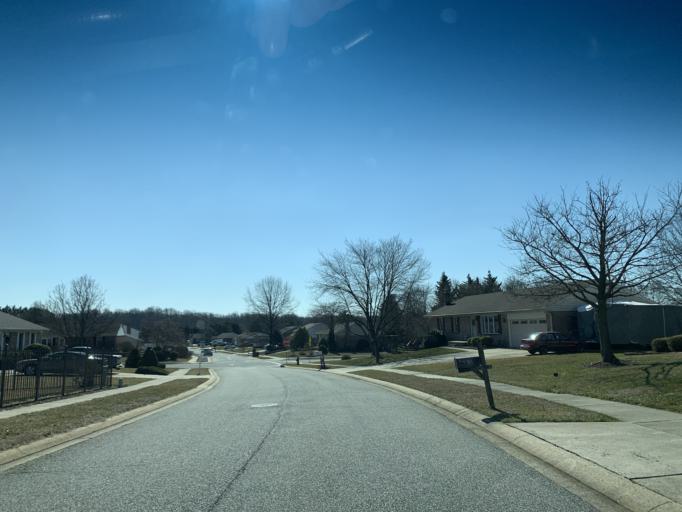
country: US
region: Maryland
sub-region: Harford County
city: South Bel Air
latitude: 39.5427
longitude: -76.2976
